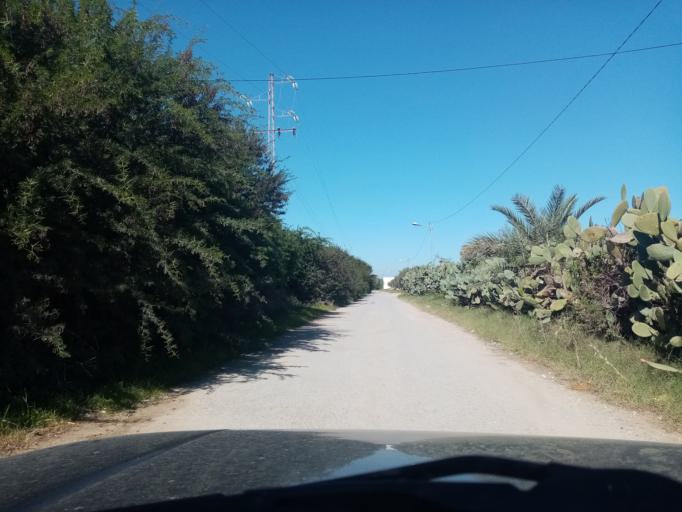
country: TN
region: Nabul
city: Bu `Urqub
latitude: 36.5681
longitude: 10.5794
